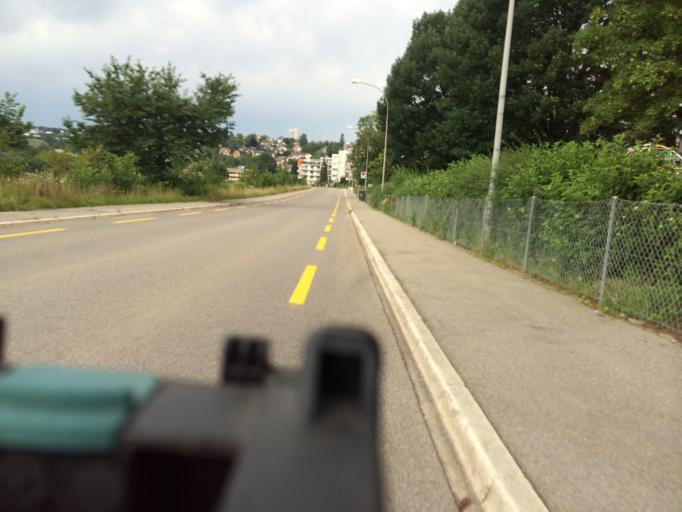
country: CH
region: Bern
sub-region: Bern-Mittelland District
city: Zollikofen
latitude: 46.9839
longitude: 7.4566
